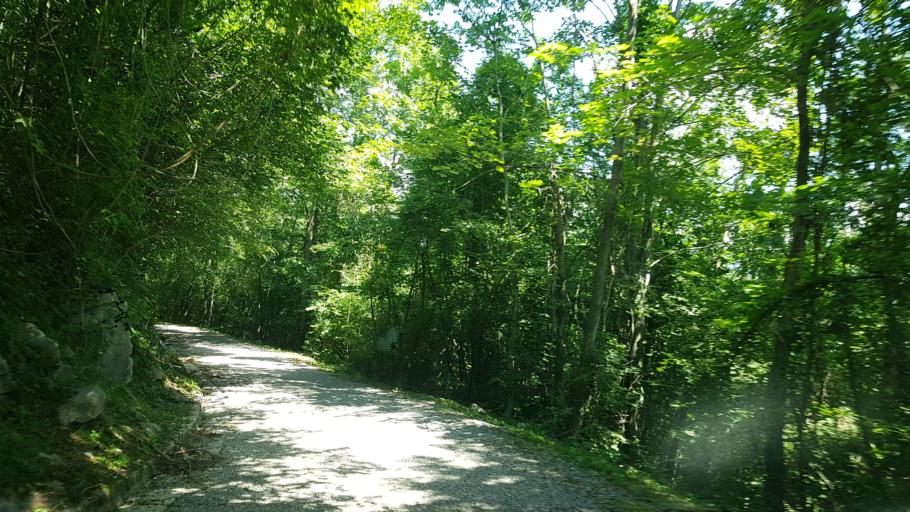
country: IT
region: Friuli Venezia Giulia
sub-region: Provincia di Udine
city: Nimis
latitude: 46.2369
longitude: 13.2655
